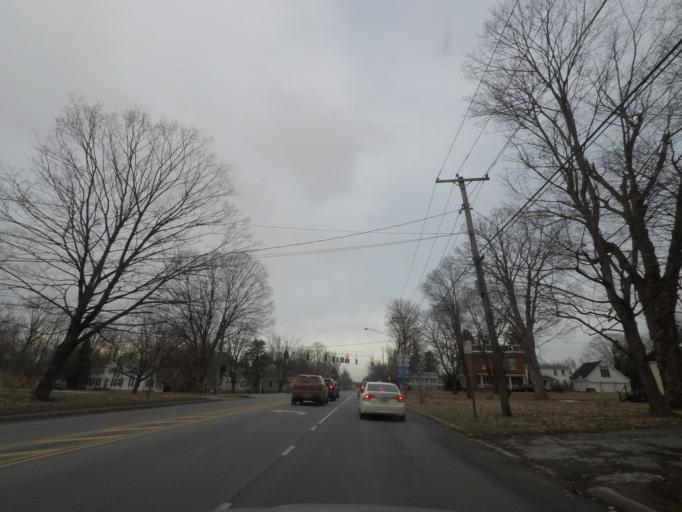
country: US
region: New York
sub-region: Madison County
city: Oneida
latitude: 43.0782
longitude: -75.6356
